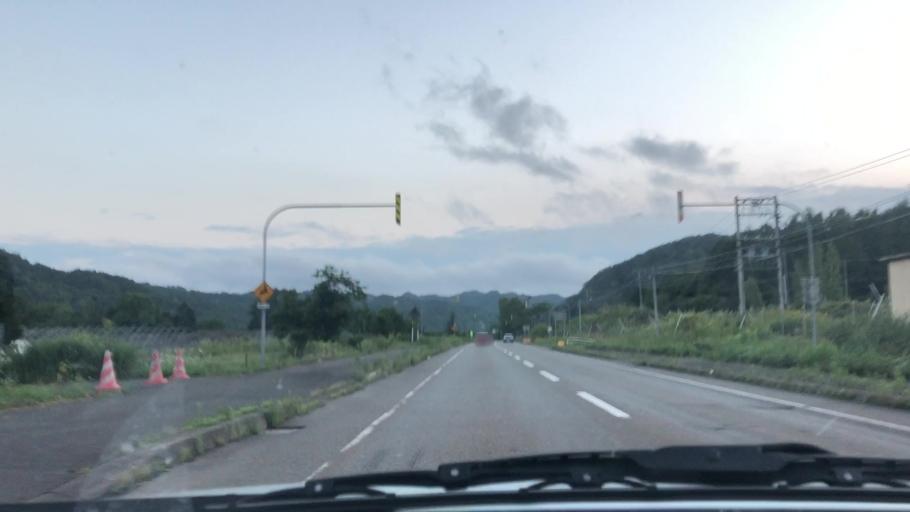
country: JP
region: Hokkaido
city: Chitose
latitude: 42.9147
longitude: 142.0248
